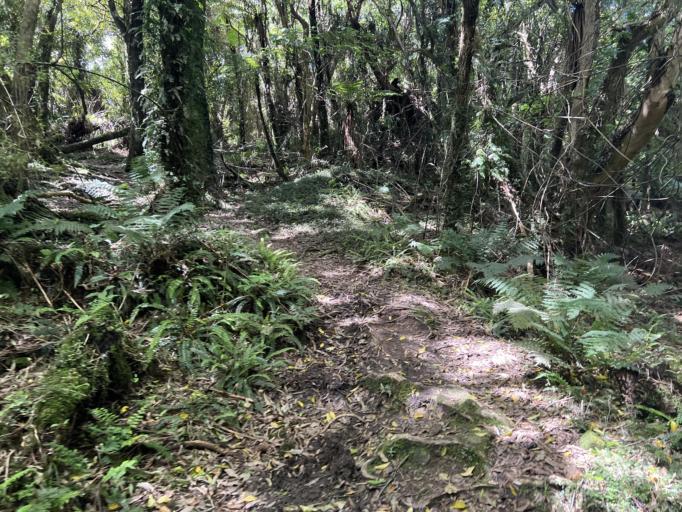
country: NZ
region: Wellington
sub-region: Kapiti Coast District
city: Paraparaumu
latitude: -40.8800
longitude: 175.0905
